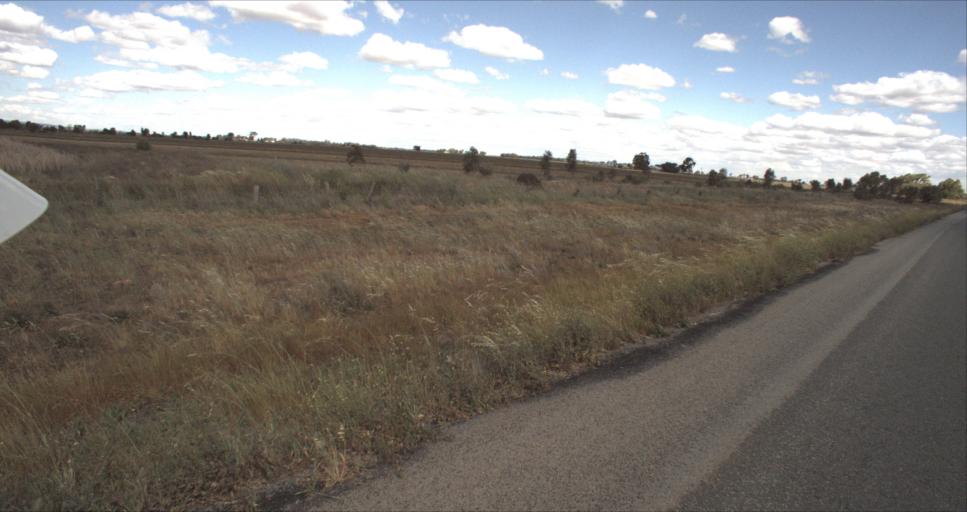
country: AU
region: New South Wales
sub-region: Leeton
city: Leeton
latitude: -34.4416
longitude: 146.2563
